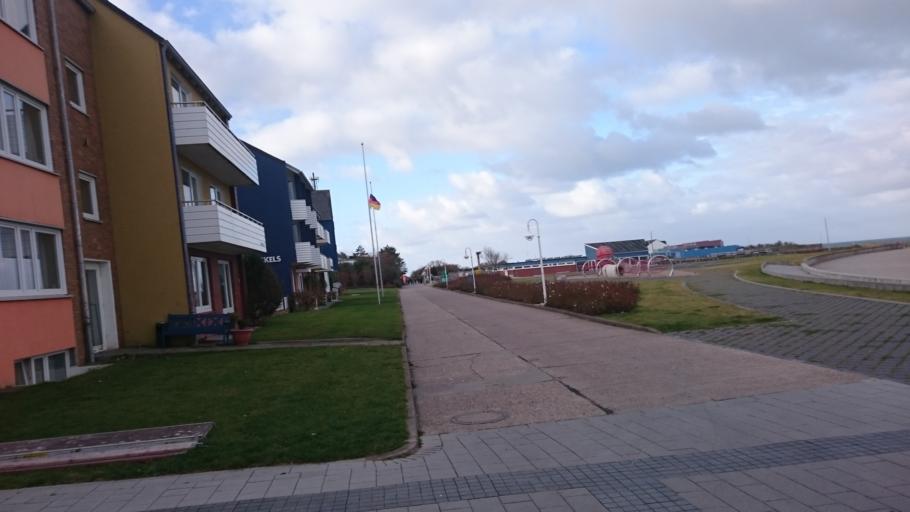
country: DE
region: Schleswig-Holstein
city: Helgoland
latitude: 54.1819
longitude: 7.8907
